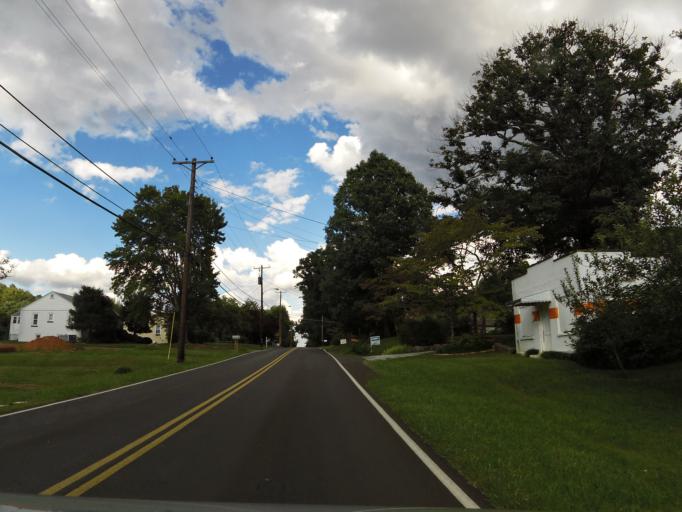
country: US
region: Tennessee
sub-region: Knox County
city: Knoxville
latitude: 36.0220
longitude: -83.8989
